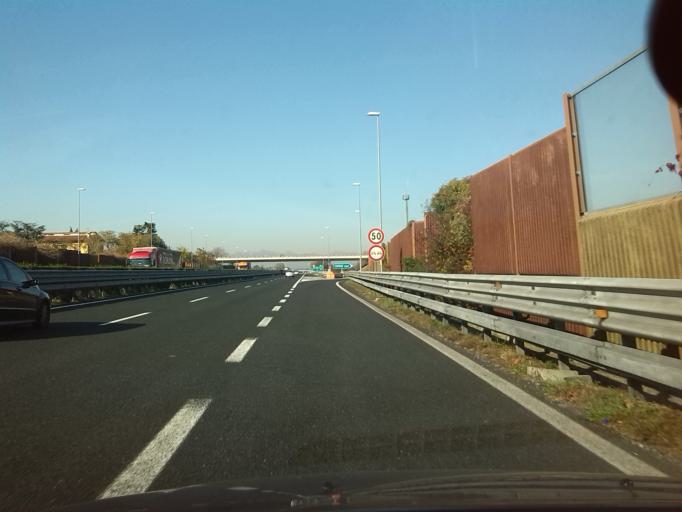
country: IT
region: Friuli Venezia Giulia
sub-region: Provincia di Udine
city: Zugliano-Terenzano-Cargnacco
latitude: 46.0075
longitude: 13.2245
